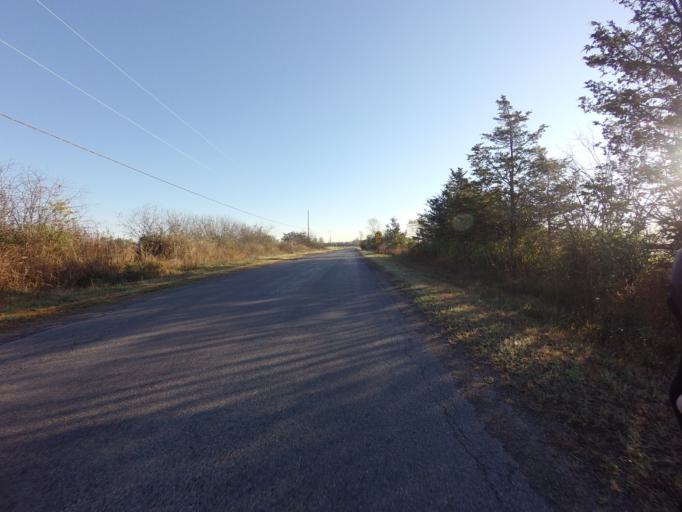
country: CA
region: Ontario
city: Quinte West
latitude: 44.0144
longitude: -77.5014
